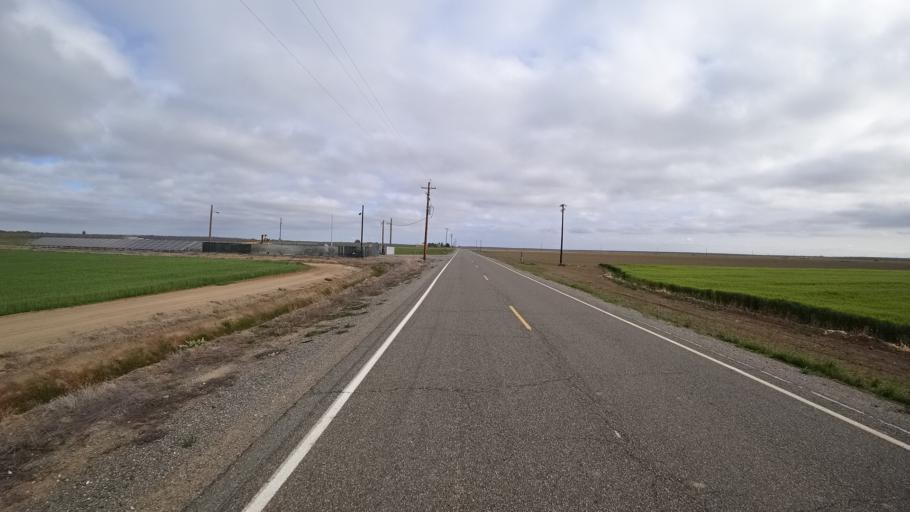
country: US
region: California
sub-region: Colusa County
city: Colusa
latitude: 39.4305
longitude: -121.9669
